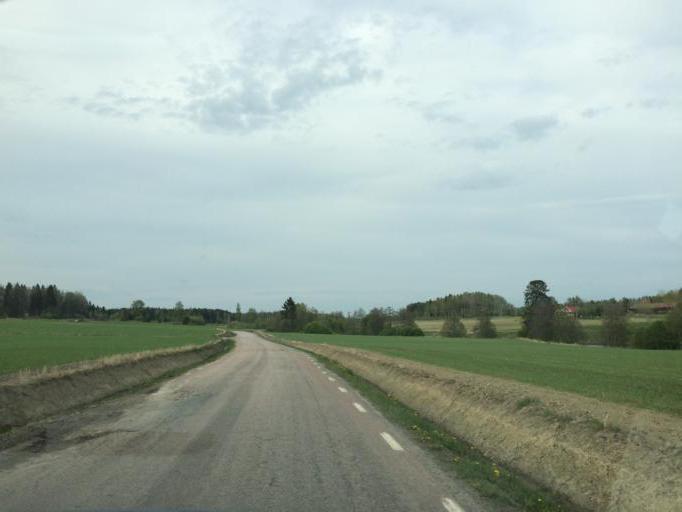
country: SE
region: Vaestmanland
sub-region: Kopings Kommun
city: Koping
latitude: 59.5969
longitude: 16.0023
